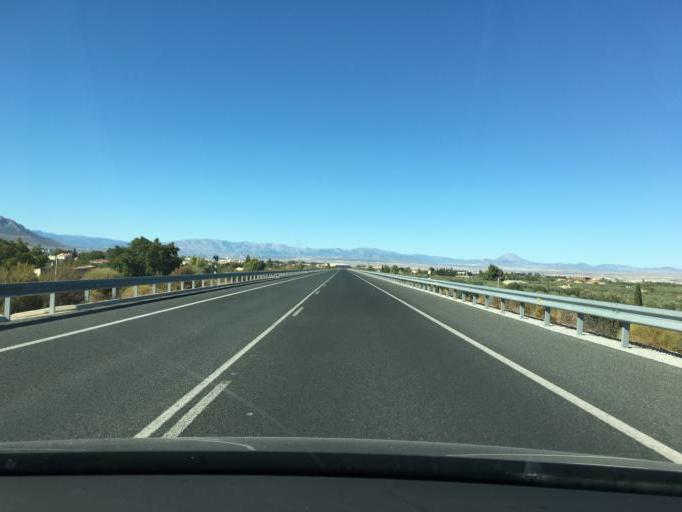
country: ES
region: Andalusia
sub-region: Provincia de Granada
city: Baza
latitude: 37.4919
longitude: -2.7399
